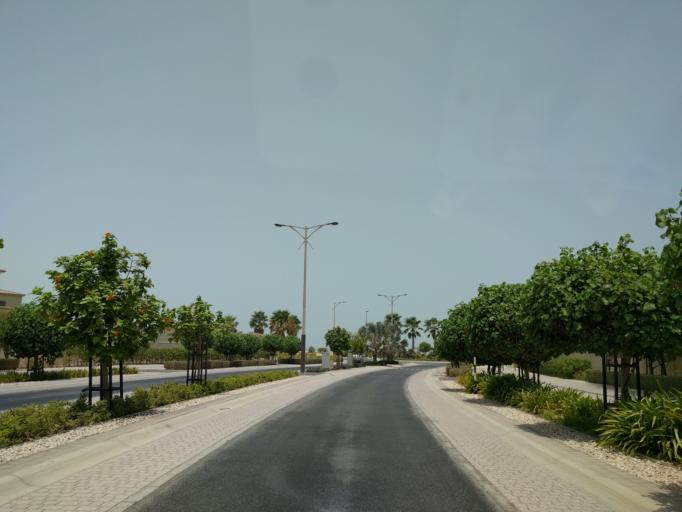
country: AE
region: Abu Dhabi
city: Abu Dhabi
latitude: 24.5533
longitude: 54.4493
